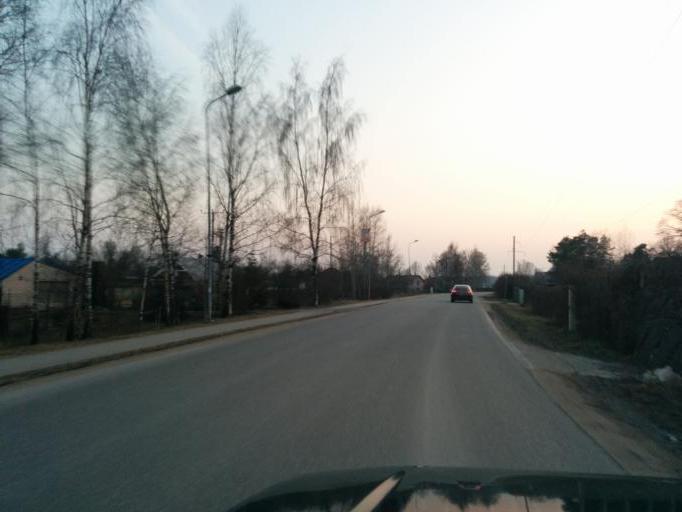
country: LV
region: Kekava
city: Balozi
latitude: 56.8604
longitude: 24.0773
